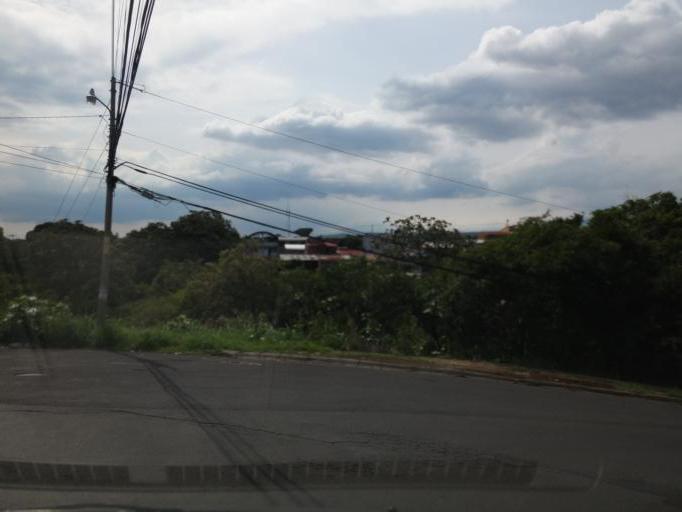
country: CR
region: Alajuela
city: Alajuela
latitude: 10.0128
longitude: -84.1985
